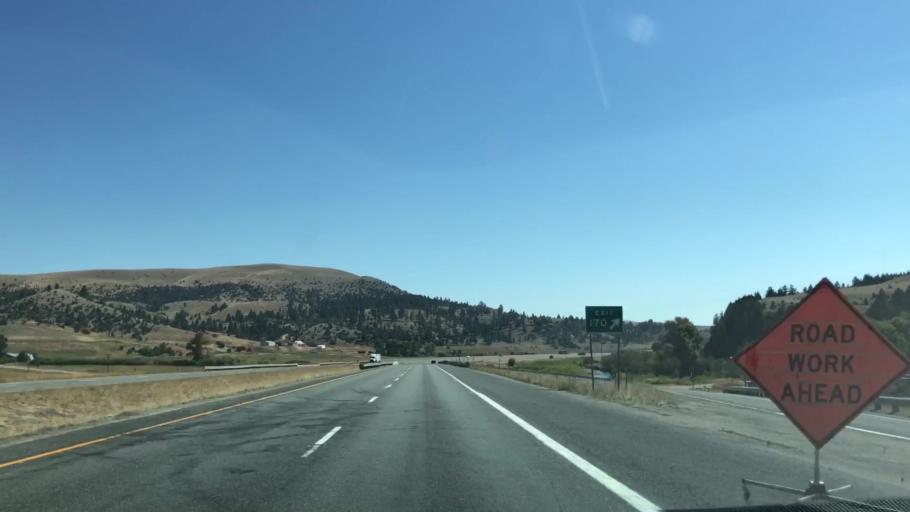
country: US
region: Montana
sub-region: Powell County
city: Deer Lodge
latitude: 46.5570
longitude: -112.8712
